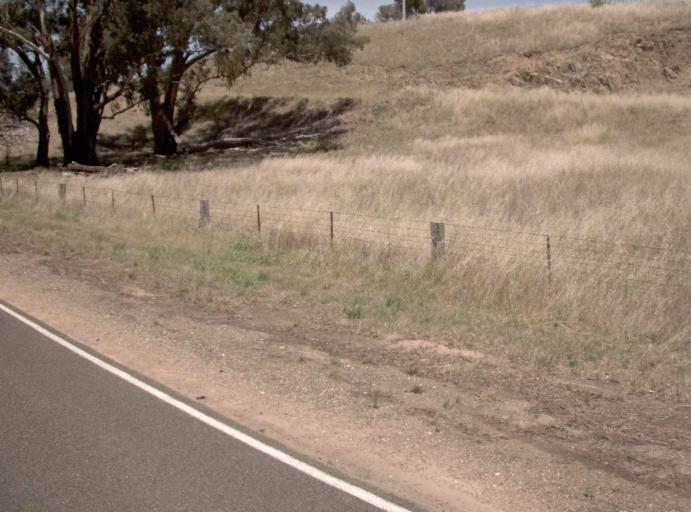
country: AU
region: Victoria
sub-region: East Gippsland
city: Bairnsdale
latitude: -37.2302
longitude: 147.7168
